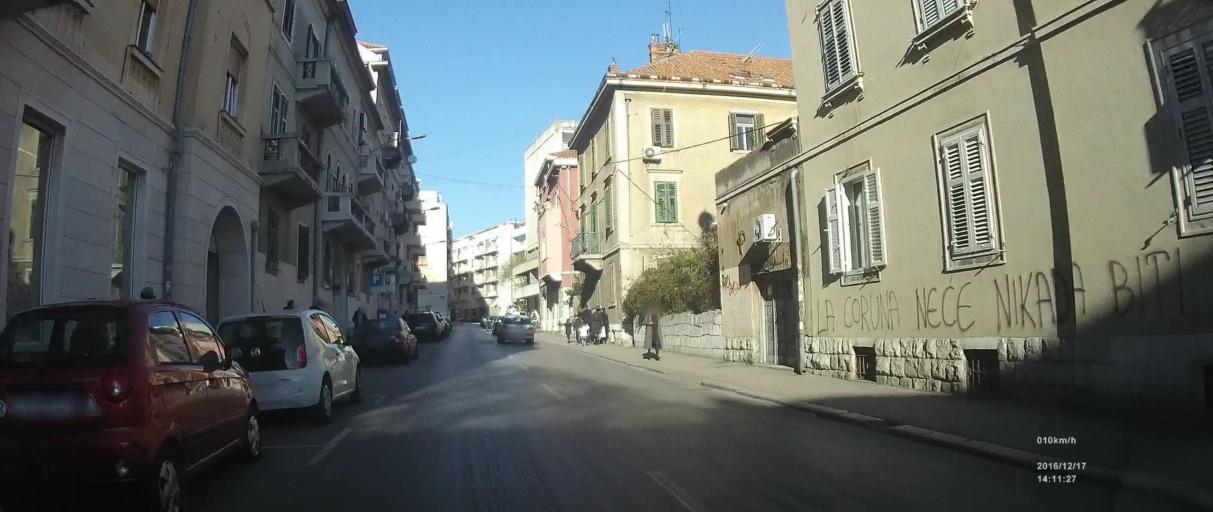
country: HR
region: Splitsko-Dalmatinska
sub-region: Grad Split
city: Split
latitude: 43.5133
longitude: 16.4378
